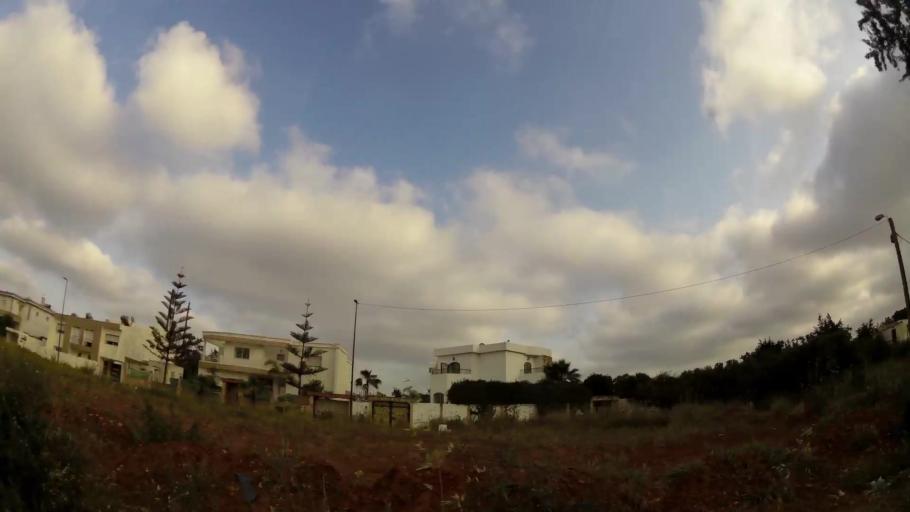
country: MA
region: Rabat-Sale-Zemmour-Zaer
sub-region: Rabat
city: Rabat
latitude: 33.9550
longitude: -6.8413
